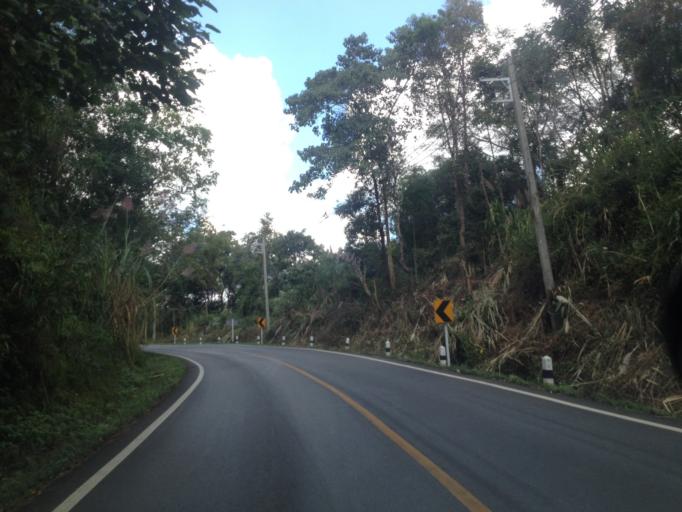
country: TH
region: Mae Hong Son
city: Ban Huai I Huak
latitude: 18.1473
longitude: 98.1541
